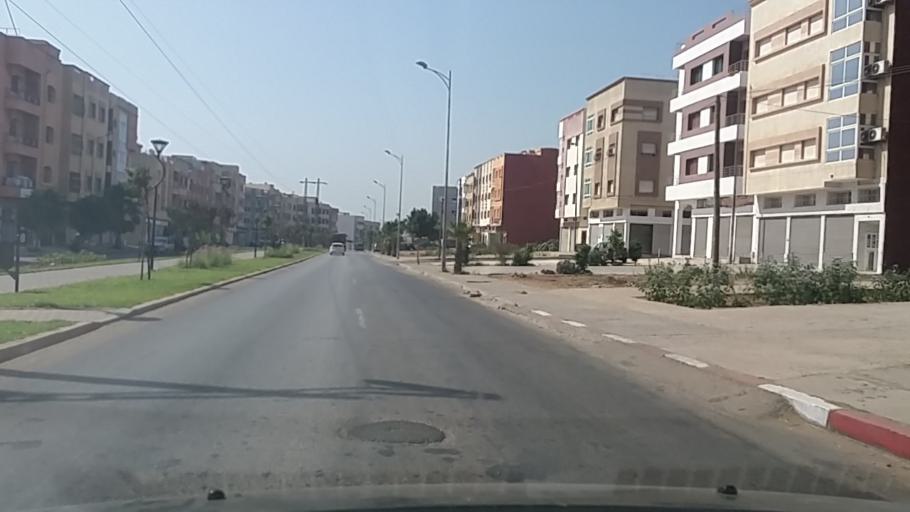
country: MA
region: Gharb-Chrarda-Beni Hssen
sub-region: Kenitra Province
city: Kenitra
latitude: 34.2541
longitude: -6.6152
